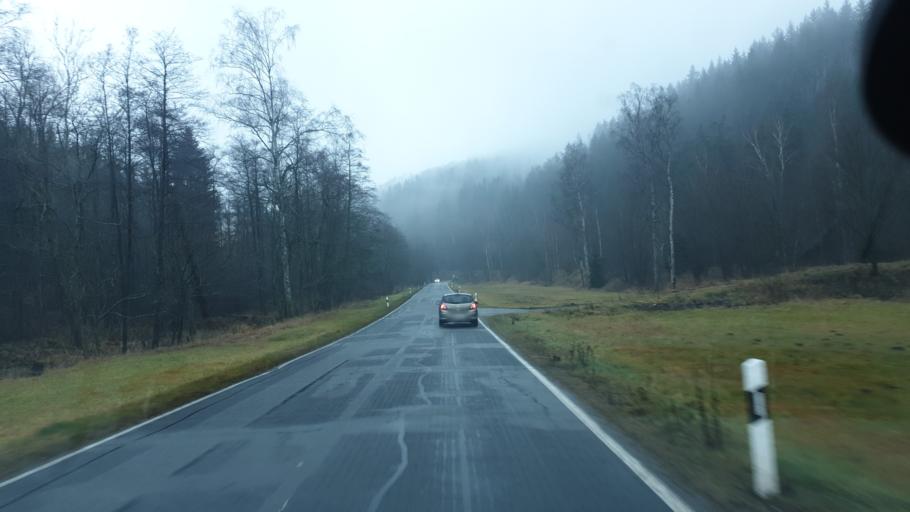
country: DE
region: Saxony
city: Seiffen
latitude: 50.6315
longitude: 13.4066
